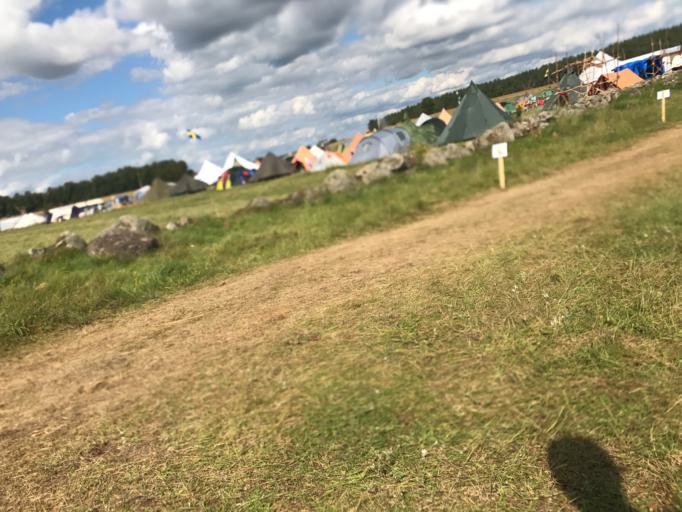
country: SE
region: Skane
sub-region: Kristianstads Kommun
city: Fjalkinge
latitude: 56.0082
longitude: 14.3025
